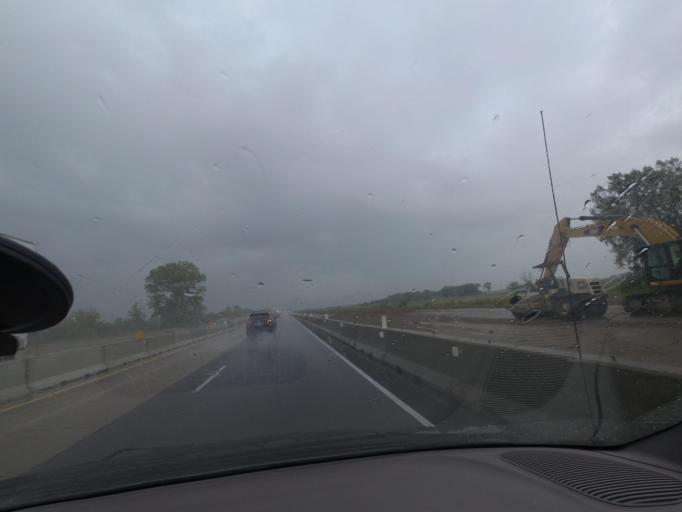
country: US
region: Indiana
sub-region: Hancock County
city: New Palestine
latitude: 39.8190
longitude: -85.8655
